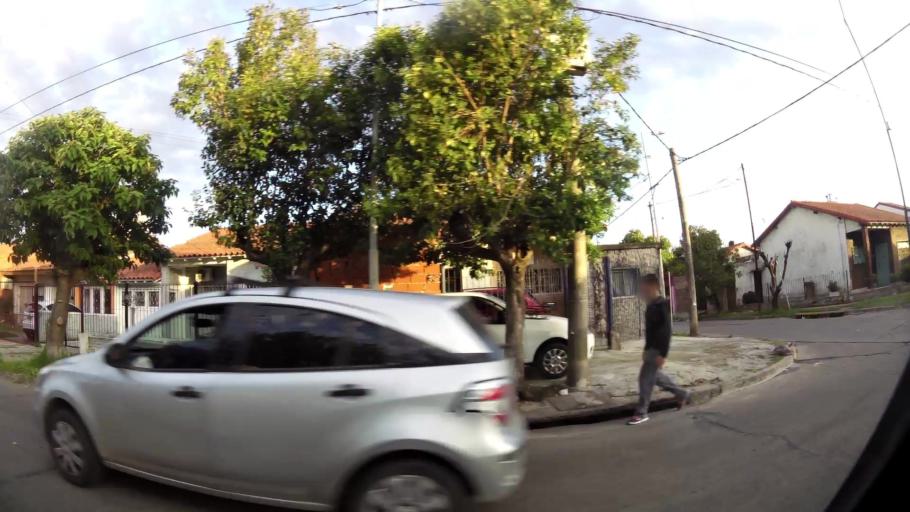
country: AR
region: Buenos Aires
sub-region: Partido de Lanus
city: Lanus
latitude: -34.7174
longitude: -58.3407
